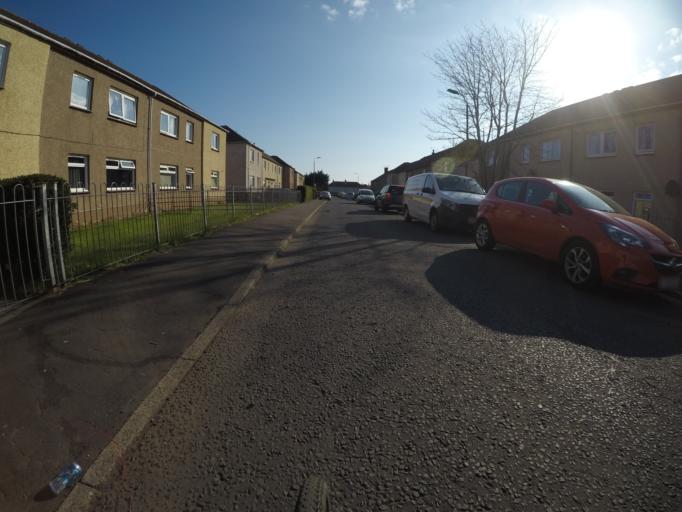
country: GB
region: Scotland
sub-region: North Ayrshire
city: Stevenston
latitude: 55.6469
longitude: -4.7497
